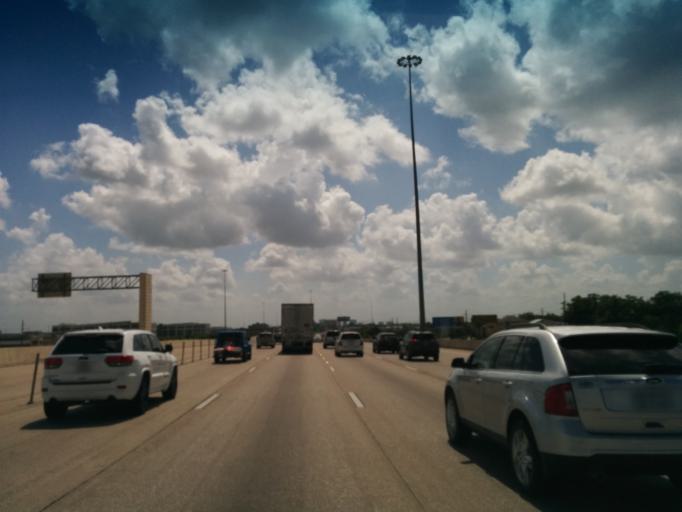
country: US
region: Texas
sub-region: Fort Bend County
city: Cinco Ranch
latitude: 29.7848
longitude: -95.6878
